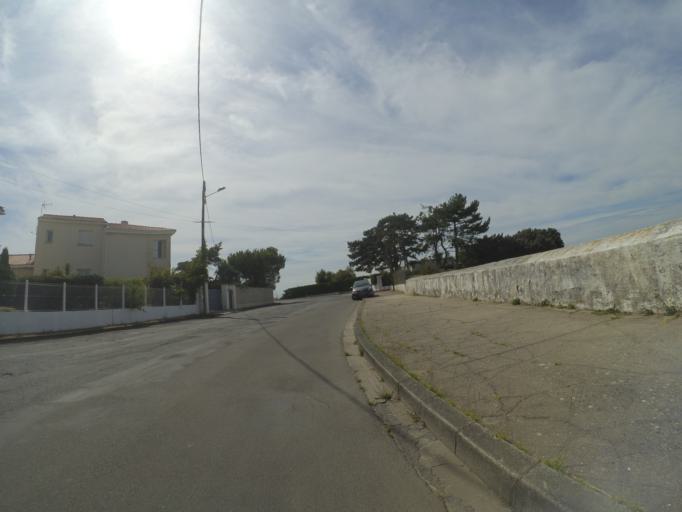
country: FR
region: Poitou-Charentes
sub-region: Departement de la Charente-Maritime
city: Saint-Georges-de-Didonne
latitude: 45.6033
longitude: -1.0126
